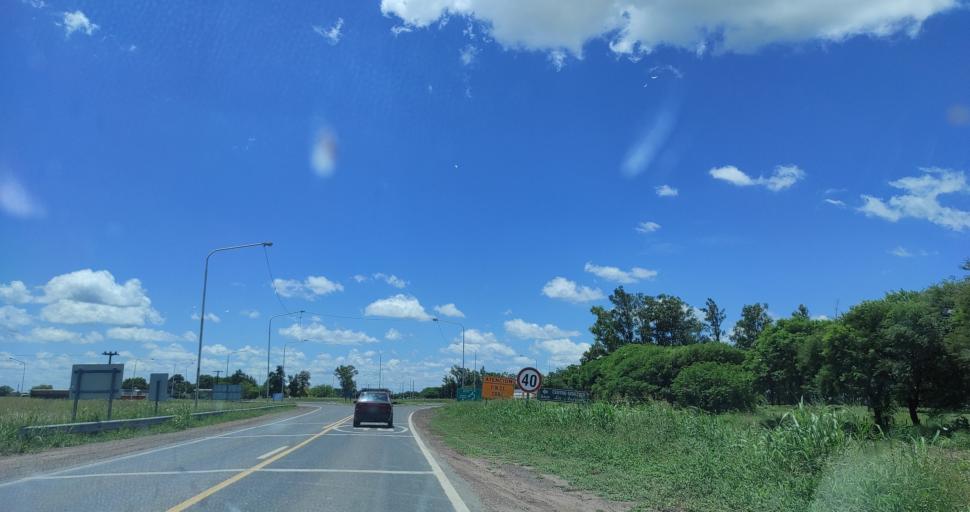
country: AR
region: Chaco
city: Avia Terai
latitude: -26.7071
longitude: -60.7490
